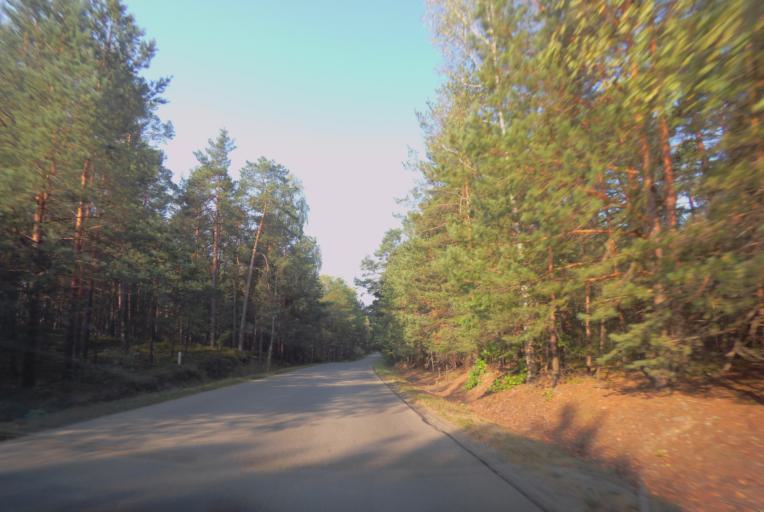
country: PL
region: Subcarpathian Voivodeship
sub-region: Powiat nizanski
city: Harasiuki
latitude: 50.5105
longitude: 22.4284
